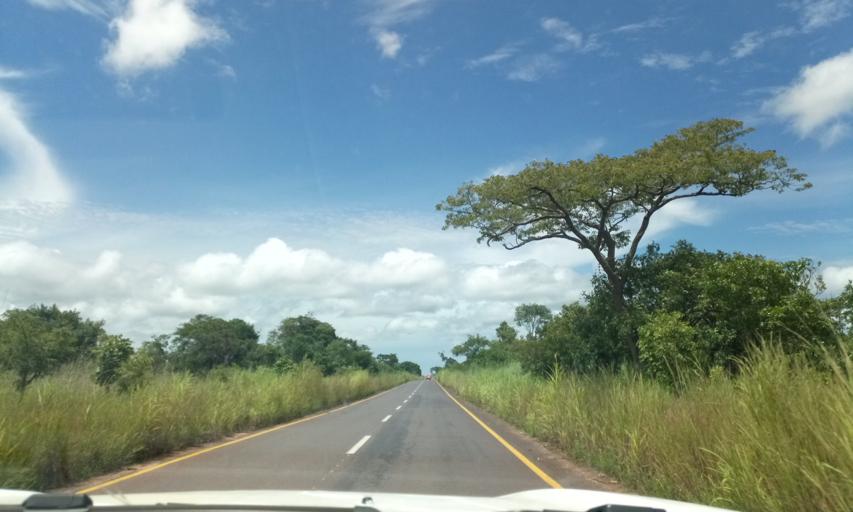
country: CD
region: Katanga
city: Lubumbashi
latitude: -11.1109
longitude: 27.9693
